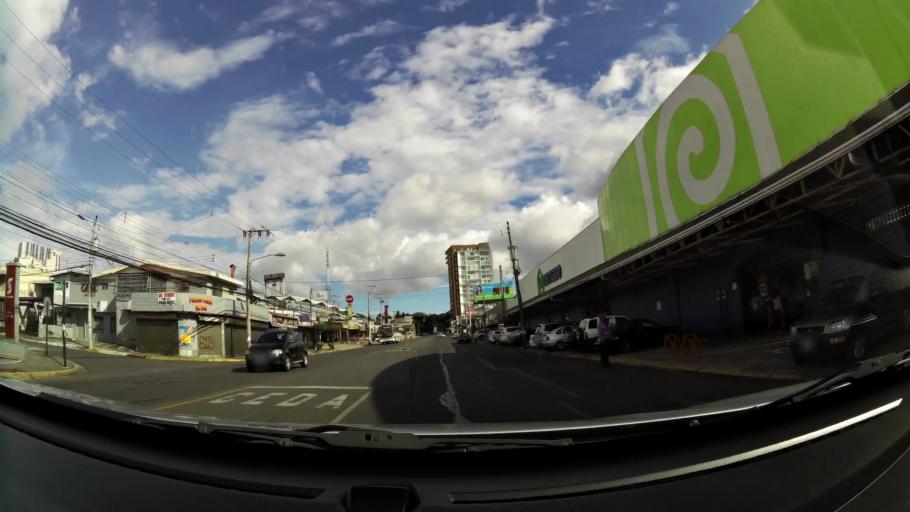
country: CR
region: San Jose
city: San Rafael
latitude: 9.9370
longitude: -84.1129
